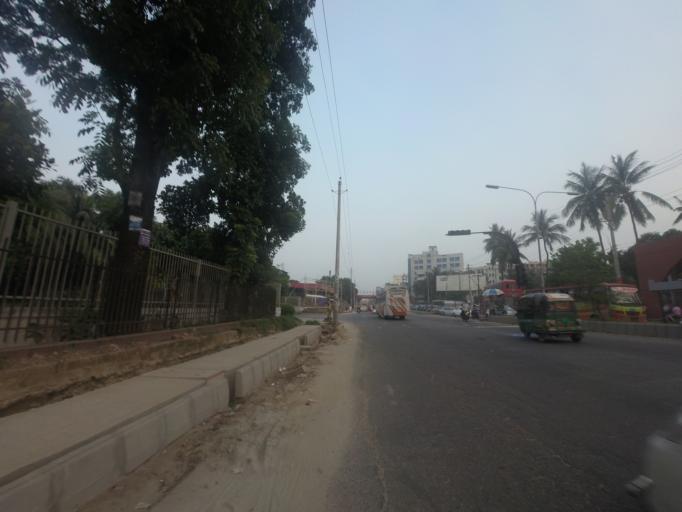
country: BD
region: Dhaka
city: Azimpur
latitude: 23.7610
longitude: 90.3727
